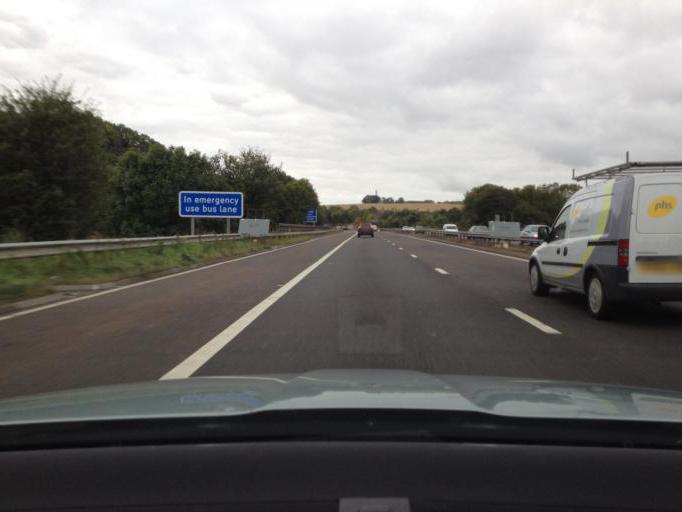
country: GB
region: Scotland
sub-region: Fife
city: Inverkeithing
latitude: 56.0375
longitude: -3.4075
